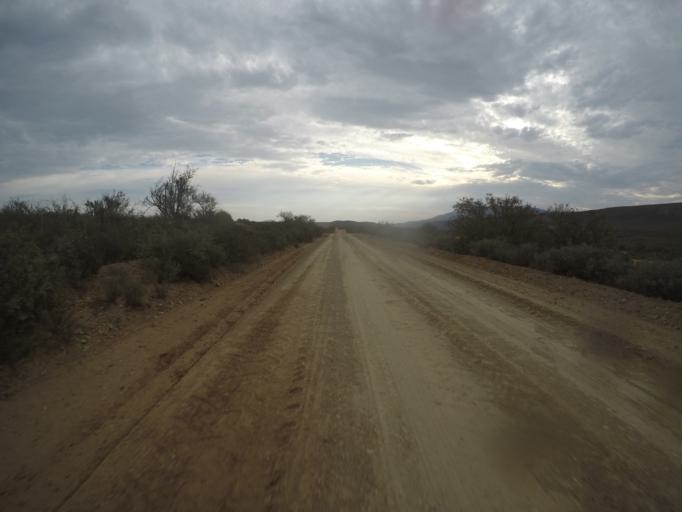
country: ZA
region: Eastern Cape
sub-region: Cacadu District Municipality
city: Willowmore
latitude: -33.4919
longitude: 23.5880
